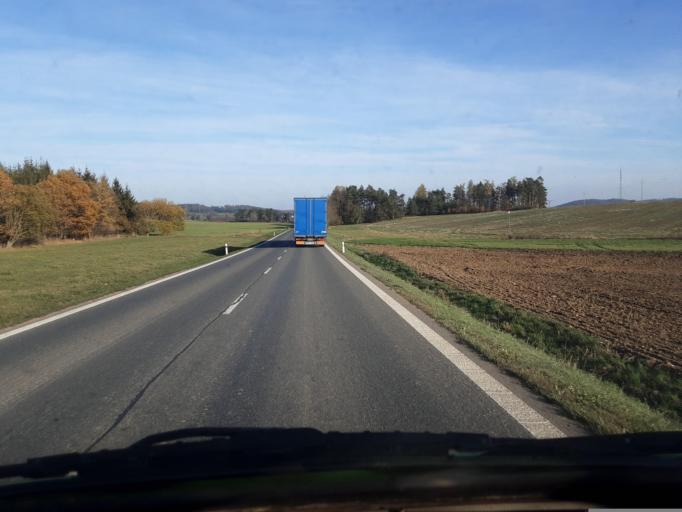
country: CZ
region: Plzensky
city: Horazd'ovice
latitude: 49.3258
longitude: 13.6237
